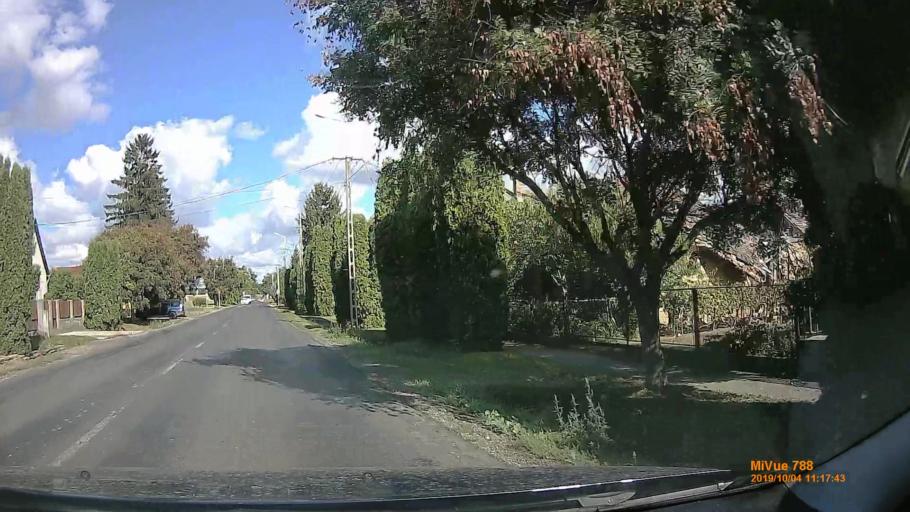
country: HU
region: Somogy
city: Kaposvar
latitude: 46.4653
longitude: 17.8044
